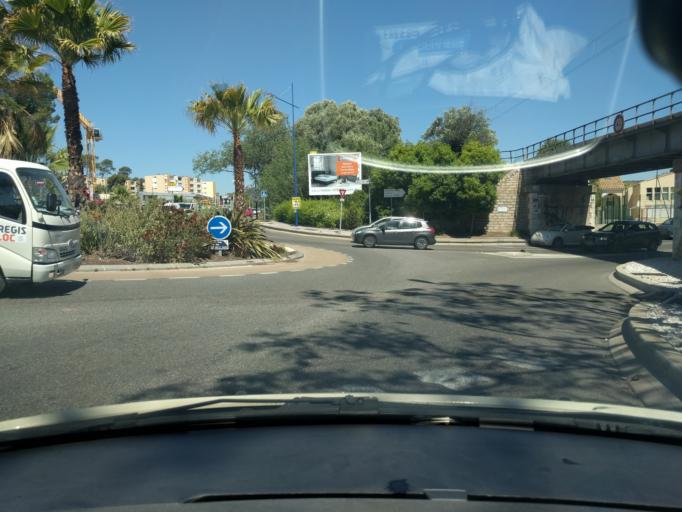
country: FR
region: Provence-Alpes-Cote d'Azur
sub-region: Departement du Var
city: Hyeres
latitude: 43.1048
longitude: 6.1277
